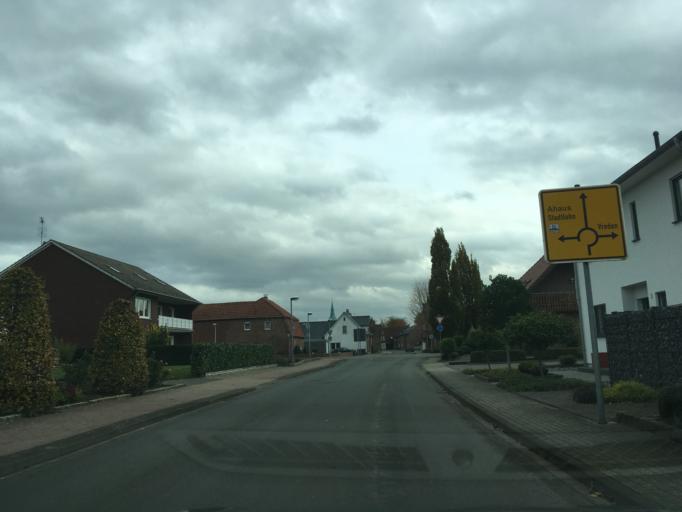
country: DE
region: North Rhine-Westphalia
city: Stadtlohn
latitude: 52.0765
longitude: 6.9127
